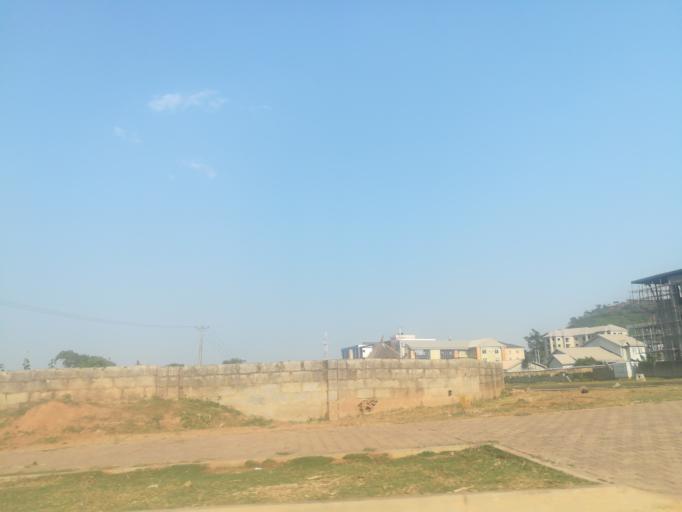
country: NG
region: Abuja Federal Capital Territory
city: Abuja
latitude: 9.0459
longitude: 7.4415
